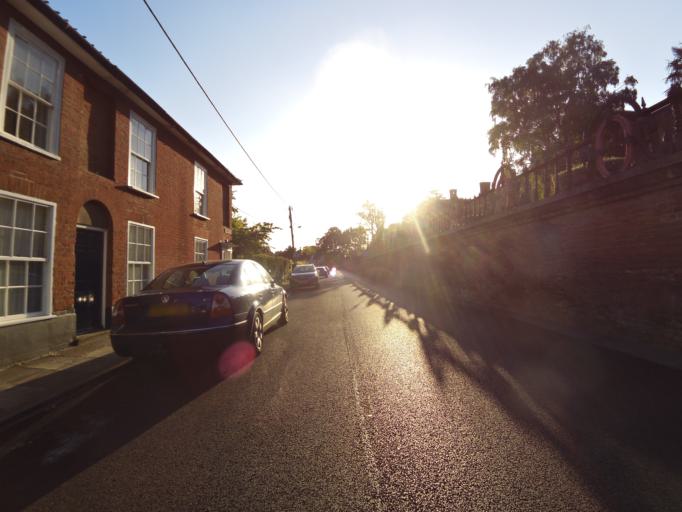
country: GB
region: England
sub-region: Suffolk
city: Woodbridge
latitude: 52.0940
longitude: 1.3067
